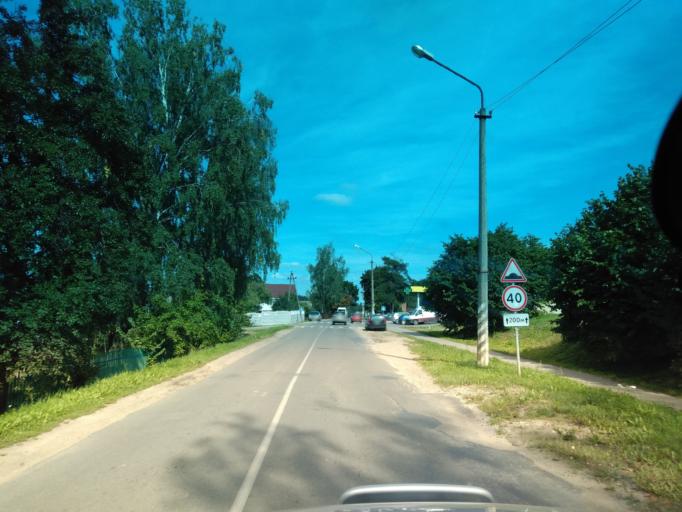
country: BY
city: Fanipol
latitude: 53.7442
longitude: 27.3311
